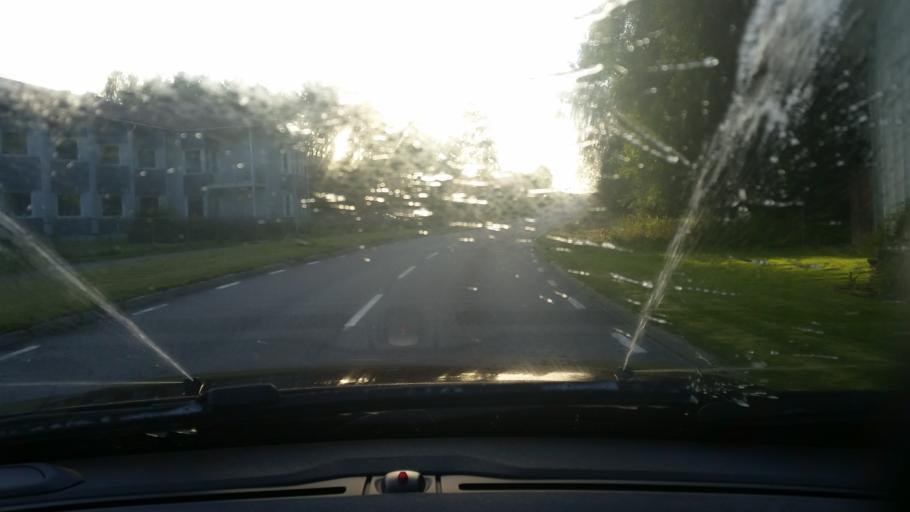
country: SE
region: Vaestra Goetaland
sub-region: Lilla Edets Kommun
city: Lodose
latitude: 58.0332
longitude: 12.1581
